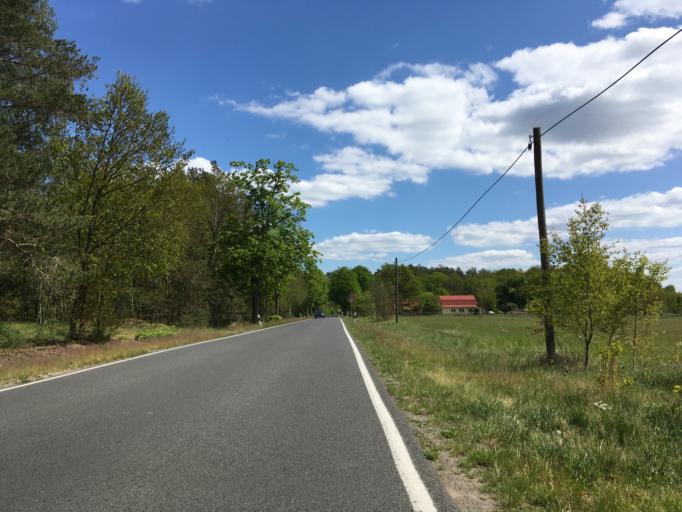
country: DE
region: Brandenburg
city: Wandlitz
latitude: 52.7855
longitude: 13.4100
